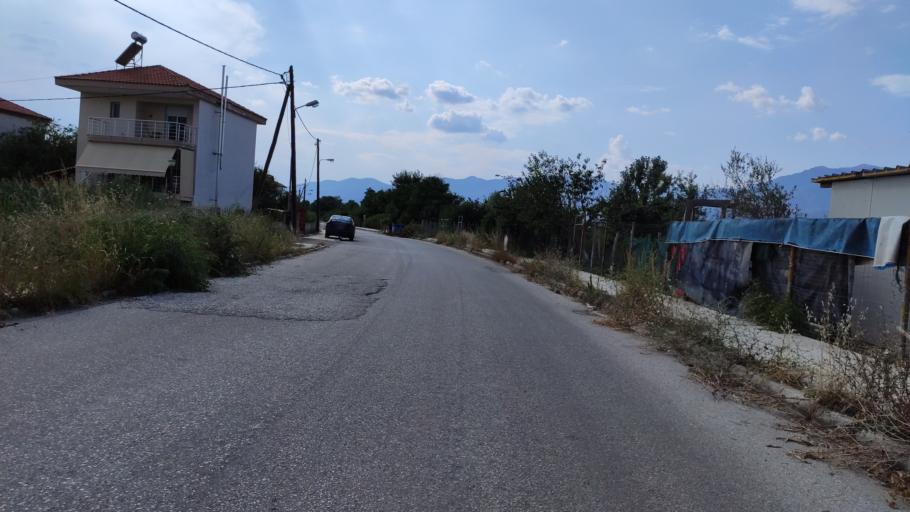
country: GR
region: East Macedonia and Thrace
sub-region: Nomos Rodopis
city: Komotini
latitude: 41.1327
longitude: 25.3977
